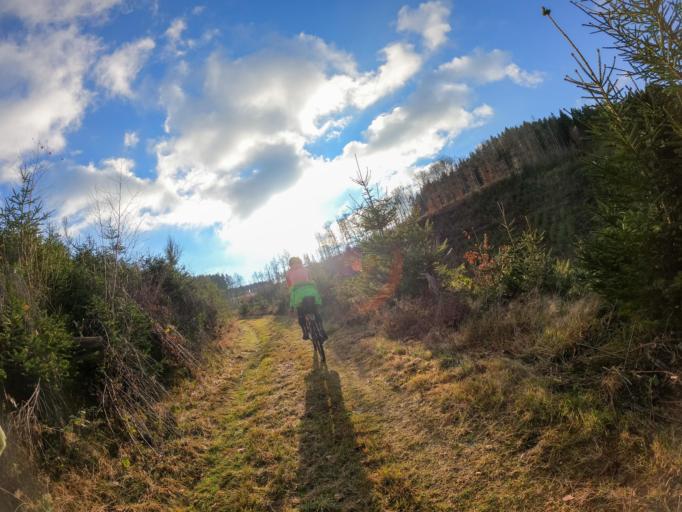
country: LU
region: Diekirch
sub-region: Canton de Wiltz
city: Winseler
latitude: 49.9886
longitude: 5.8397
